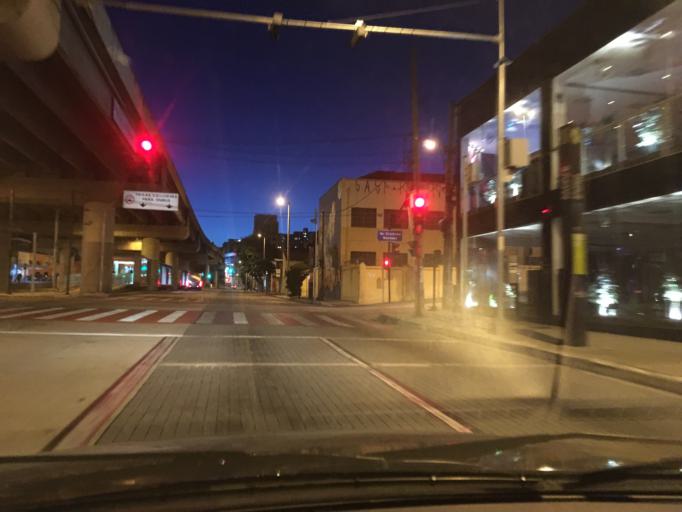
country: BR
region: Minas Gerais
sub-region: Belo Horizonte
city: Belo Horizonte
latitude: -19.9036
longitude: -43.9323
